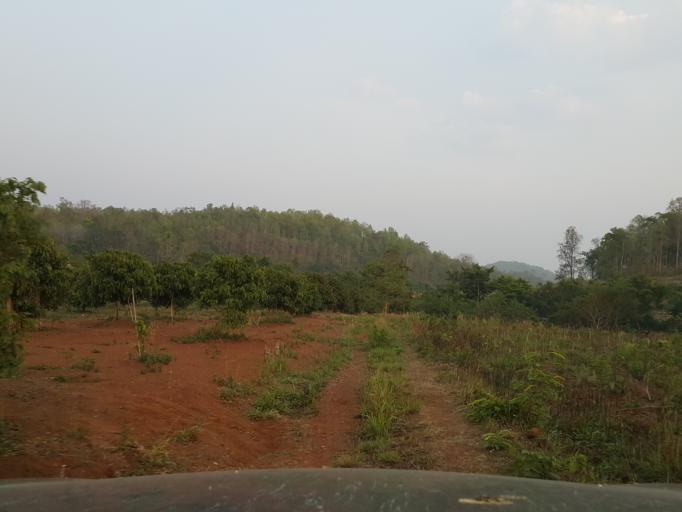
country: TH
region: Lamphun
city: Thung Hua Chang
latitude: 17.9100
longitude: 99.0757
